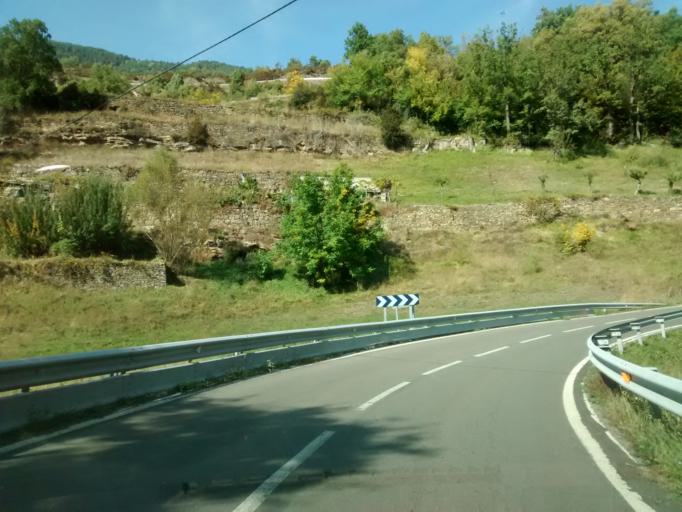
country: ES
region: Aragon
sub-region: Provincia de Huesca
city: Broto
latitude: 42.6112
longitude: -0.1244
